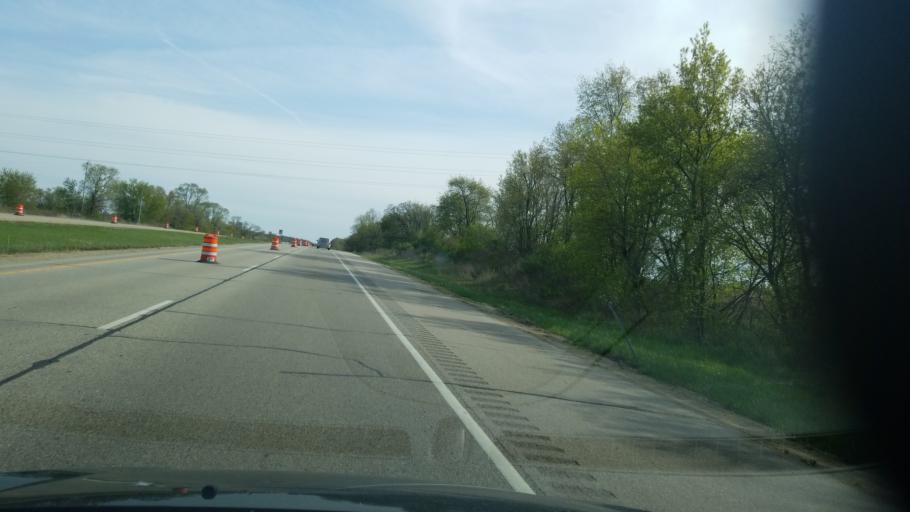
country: US
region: Wisconsin
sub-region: Dane County
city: Oregon
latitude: 42.9911
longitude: -89.3864
